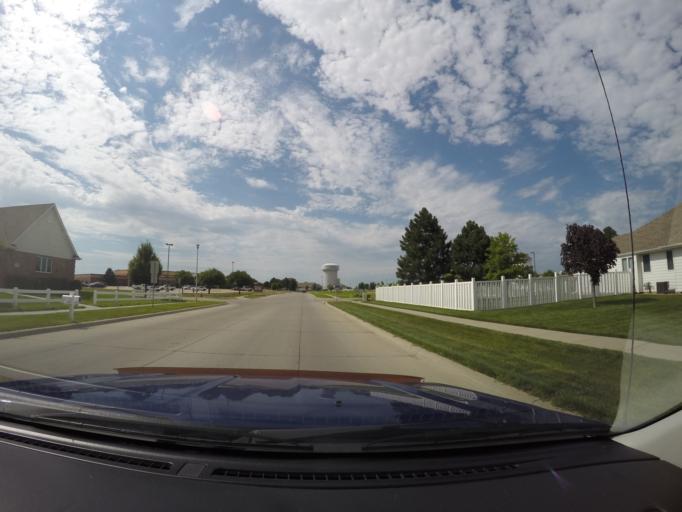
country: US
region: Nebraska
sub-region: Buffalo County
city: Kearney
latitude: 40.7175
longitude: -99.0900
